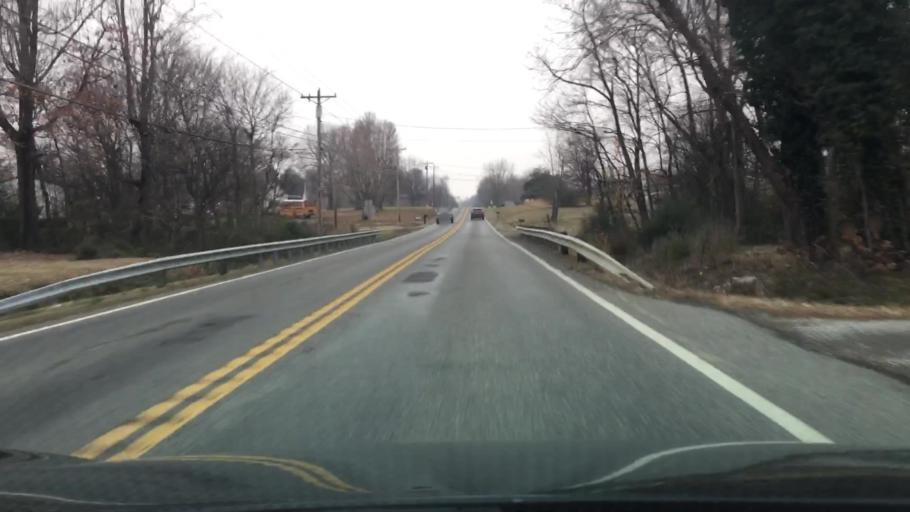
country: US
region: Kentucky
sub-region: Livingston County
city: Ledbetter
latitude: 36.9701
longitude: -88.4613
